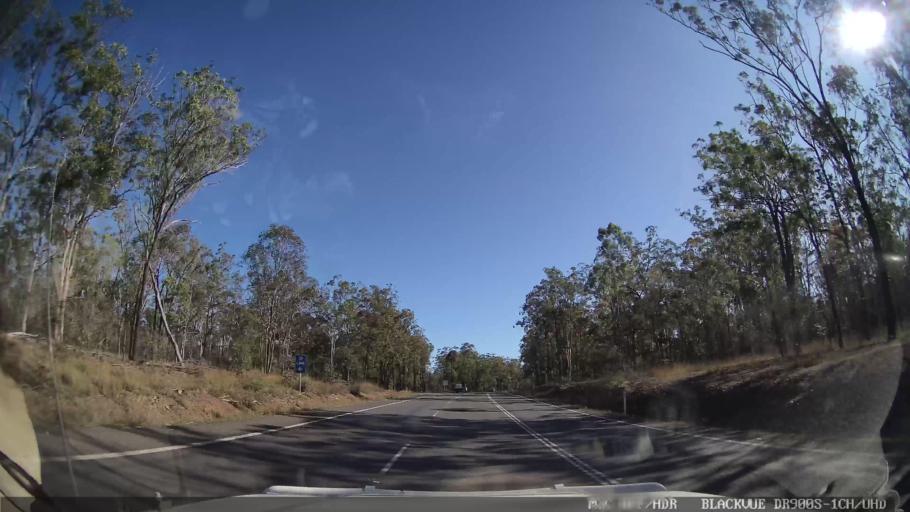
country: AU
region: Queensland
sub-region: Bundaberg
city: Childers
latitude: -25.2150
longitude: 152.0788
